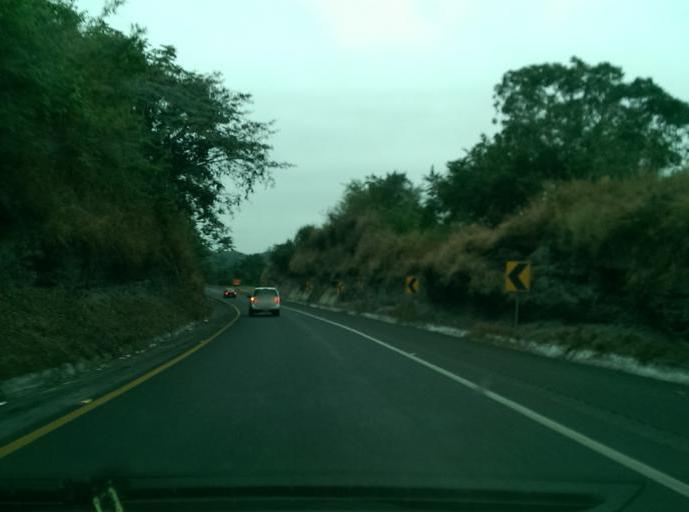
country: MX
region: Veracruz
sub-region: Tierra Blanca
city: Huixcolotla
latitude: 18.7815
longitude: -96.4602
